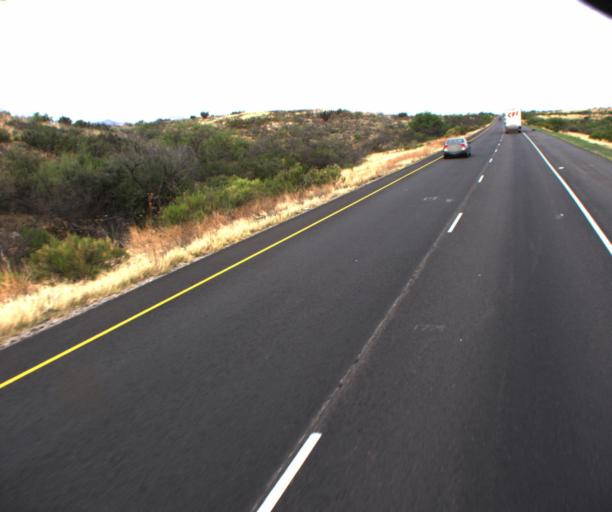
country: US
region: Arizona
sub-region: Cochise County
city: Mescal
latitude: 31.9720
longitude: -110.4811
